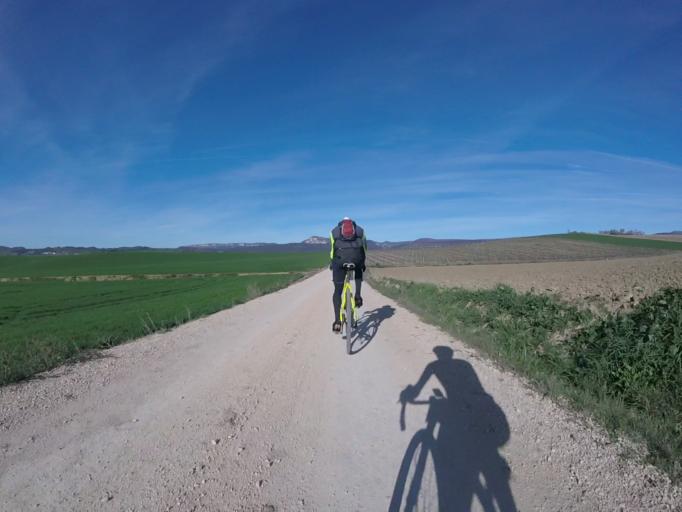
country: ES
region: Navarre
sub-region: Provincia de Navarra
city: Yerri
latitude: 42.7139
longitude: -1.9735
